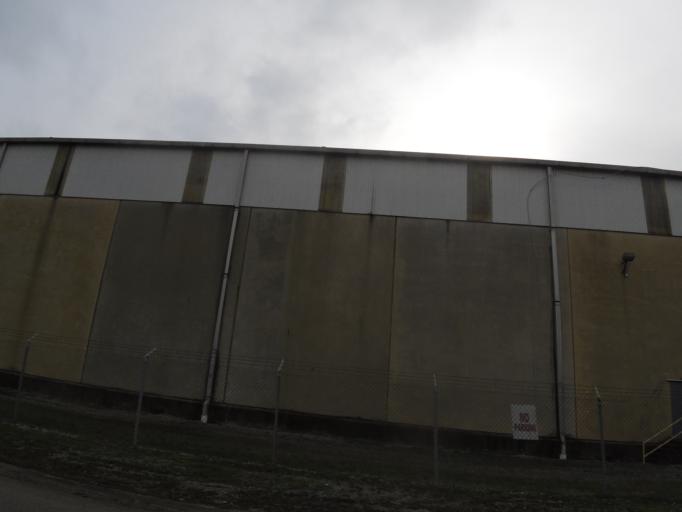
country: US
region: Alabama
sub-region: Montgomery County
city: Montgomery
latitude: 32.4072
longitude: -86.3051
